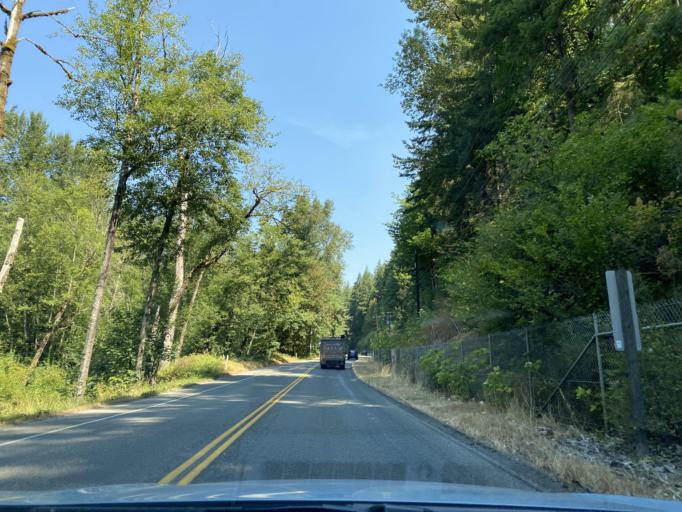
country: US
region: Washington
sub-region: Pierce County
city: McMillin
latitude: 47.1451
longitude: -122.2211
